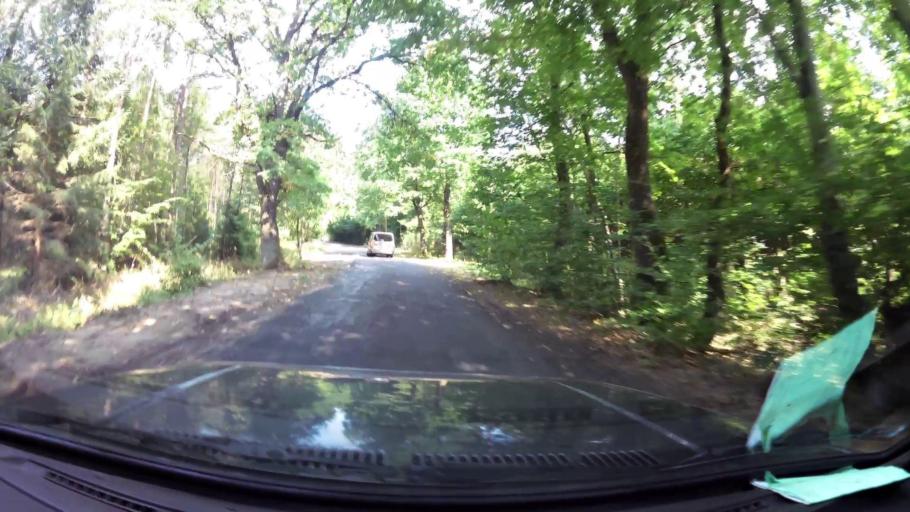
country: PL
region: West Pomeranian Voivodeship
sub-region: Powiat koszalinski
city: Bobolice
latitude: 54.1029
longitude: 16.4974
